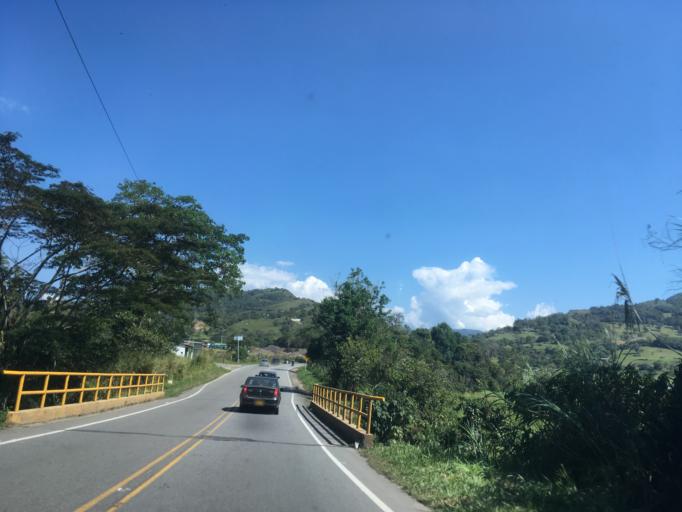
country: CO
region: Santander
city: Suaita
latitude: 6.0667
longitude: -73.4223
